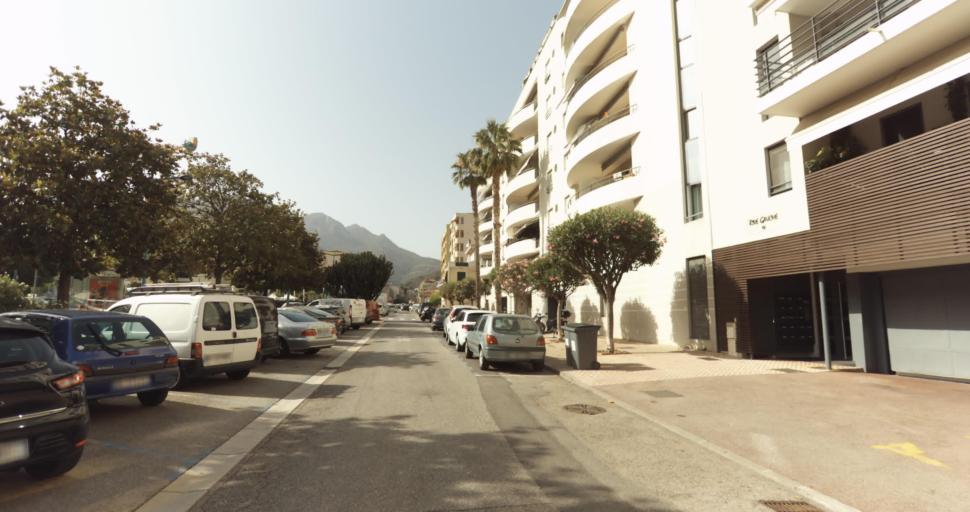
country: FR
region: Provence-Alpes-Cote d'Azur
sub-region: Departement des Alpes-Maritimes
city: Roquebrune-Cap-Martin
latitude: 43.7778
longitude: 7.4871
